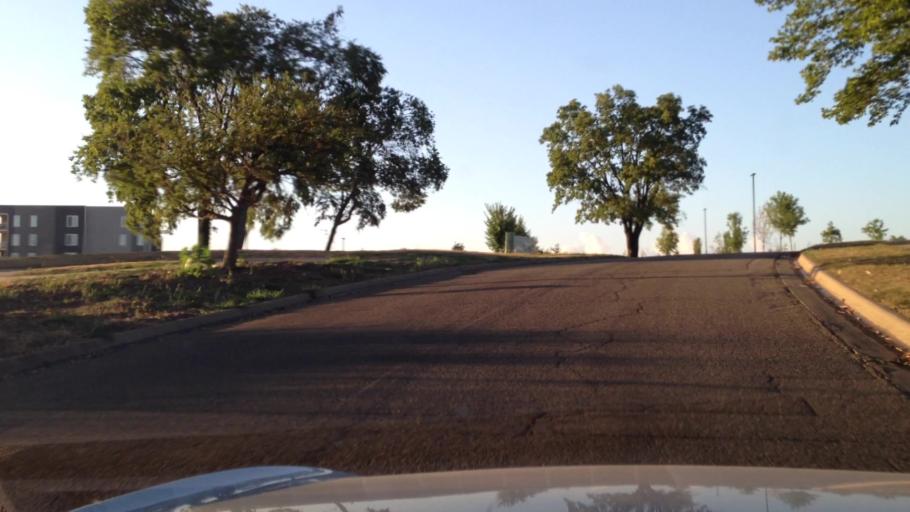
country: US
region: Kansas
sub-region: Douglas County
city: Lawrence
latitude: 38.9501
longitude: -95.2913
